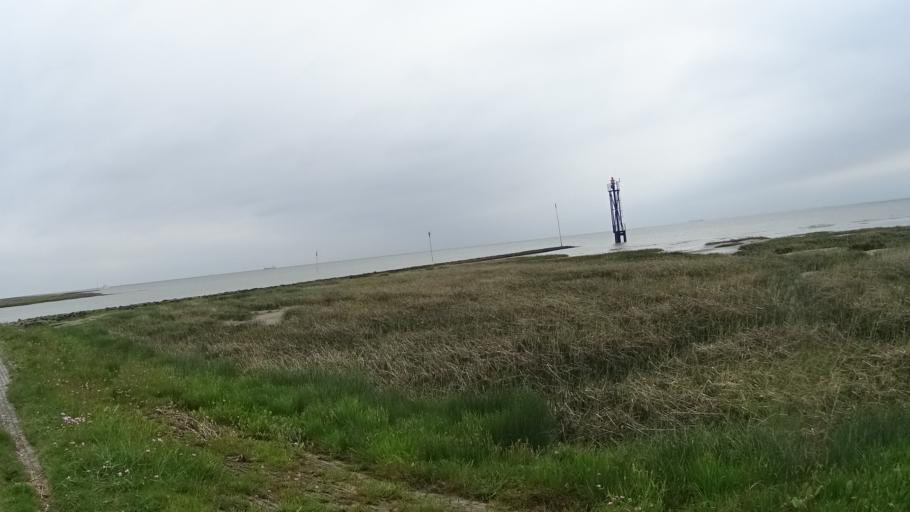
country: DE
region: Lower Saxony
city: Butjadingen
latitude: 53.5985
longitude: 8.3576
